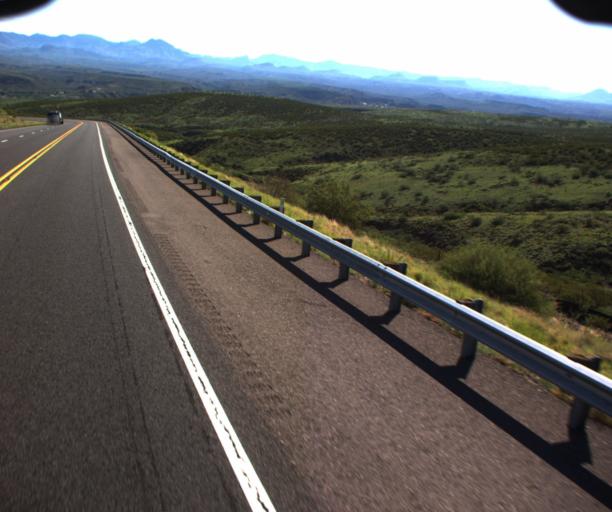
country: US
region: Arizona
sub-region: Greenlee County
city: Clifton
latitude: 32.9254
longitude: -109.2425
